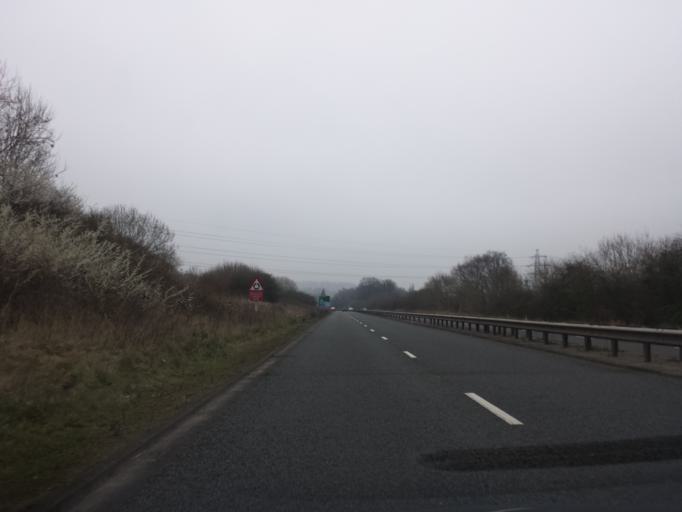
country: GB
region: England
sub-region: Bath and North East Somerset
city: Bath
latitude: 51.4005
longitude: -2.3159
